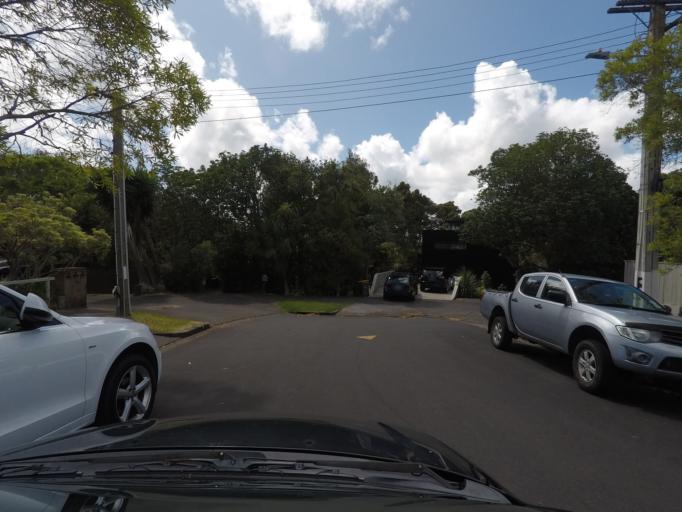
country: NZ
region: Auckland
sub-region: Auckland
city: Rosebank
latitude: -36.8584
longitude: 174.7074
